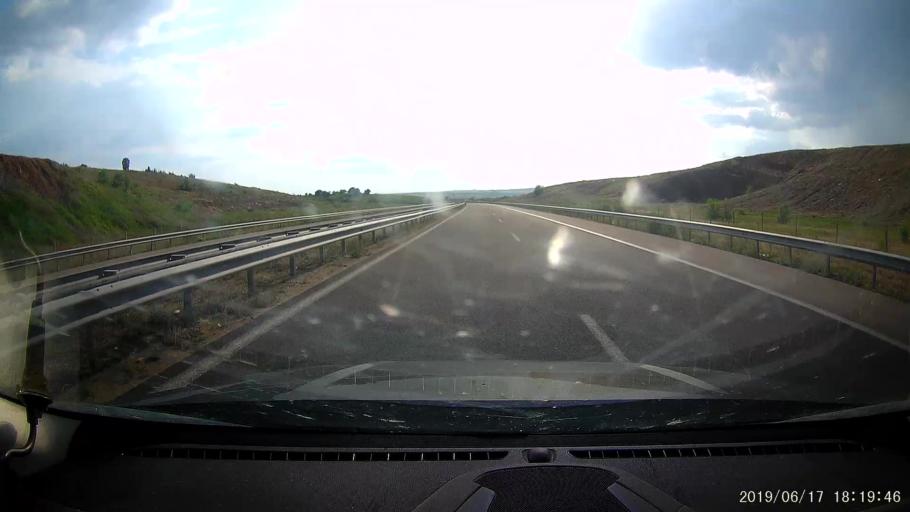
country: BG
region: Khaskovo
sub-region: Obshtina Simeonovgrad
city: Simeonovgrad
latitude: 41.9631
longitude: 25.8360
